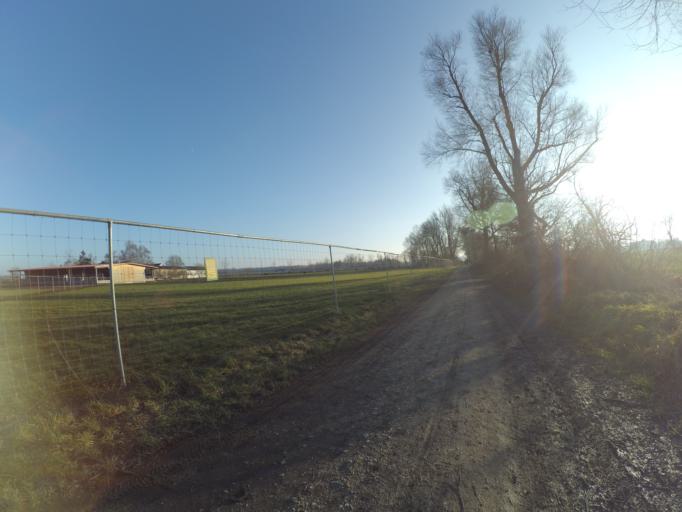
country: DE
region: Bavaria
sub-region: Swabia
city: Leipheim
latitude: 48.4692
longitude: 10.2078
